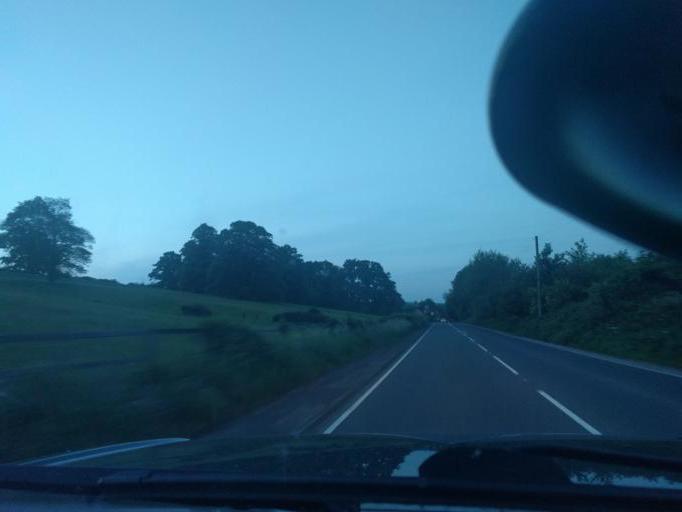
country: GB
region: England
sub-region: Wiltshire
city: Colerne
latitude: 51.4064
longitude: -2.2906
